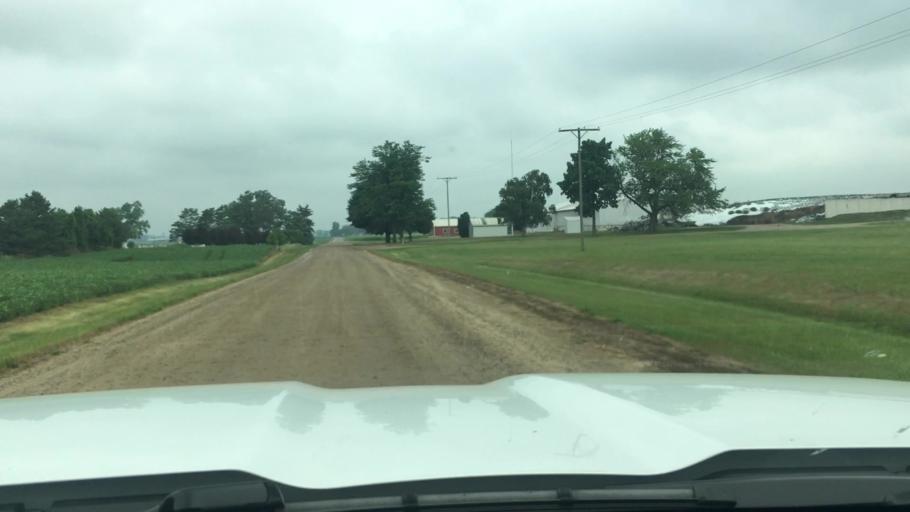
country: US
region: Michigan
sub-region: Sanilac County
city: Marlette
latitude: 43.3471
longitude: -82.9754
